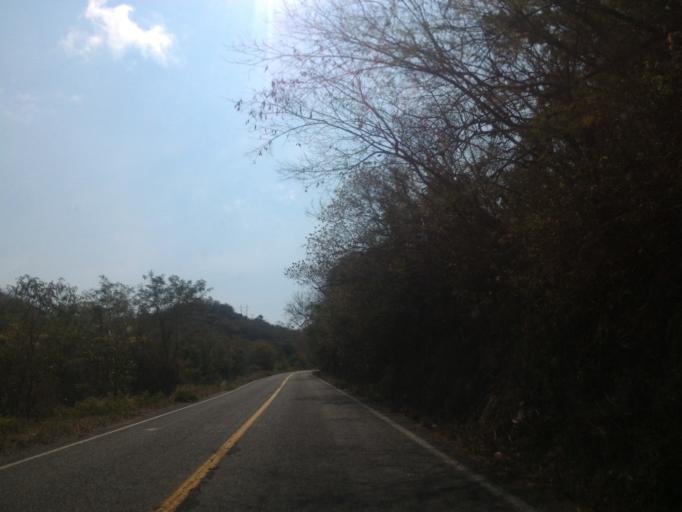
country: MX
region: Michoacan
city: Coahuayana Viejo
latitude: 18.3508
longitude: -103.4874
